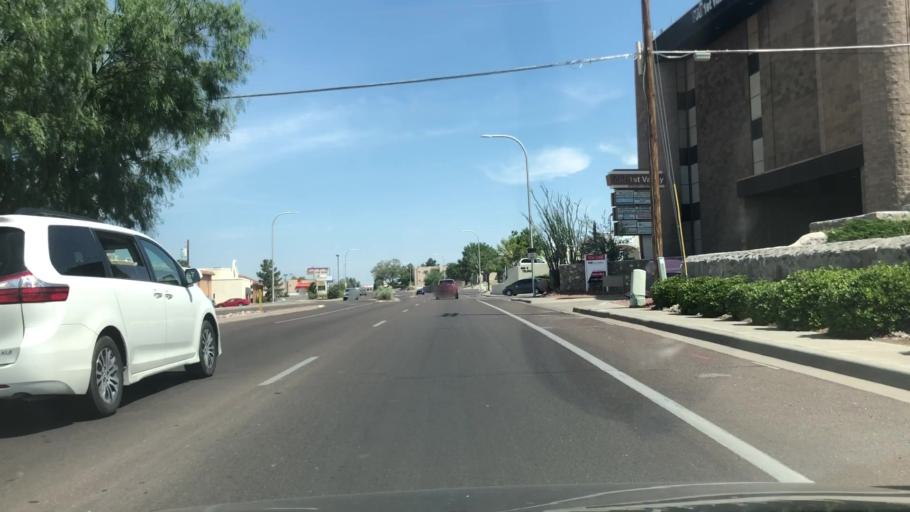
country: US
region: New Mexico
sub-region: Dona Ana County
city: University Park
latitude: 32.3053
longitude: -106.7382
